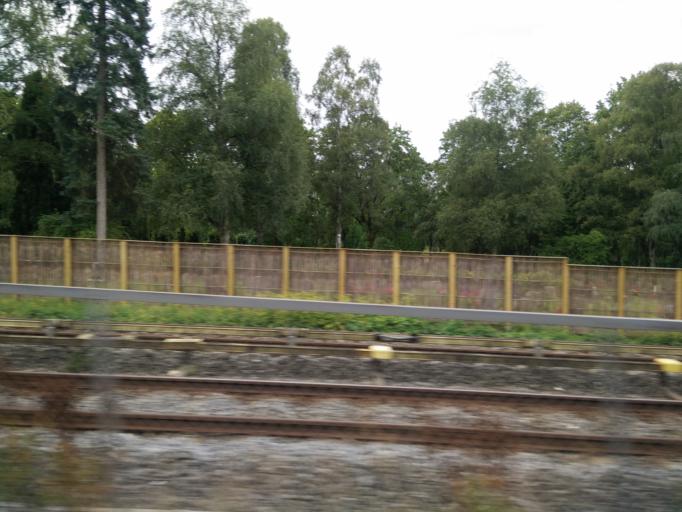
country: NO
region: Oslo
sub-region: Oslo
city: Sjolyststranda
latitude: 59.9338
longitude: 10.7009
